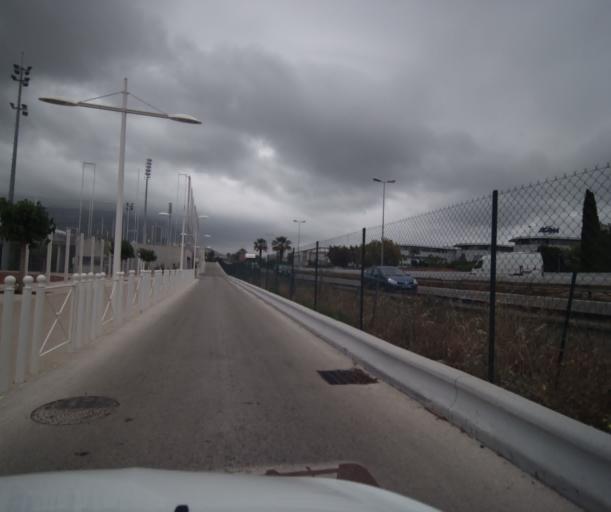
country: FR
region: Provence-Alpes-Cote d'Azur
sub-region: Departement du Var
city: La Valette-du-Var
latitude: 43.1264
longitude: 5.9732
